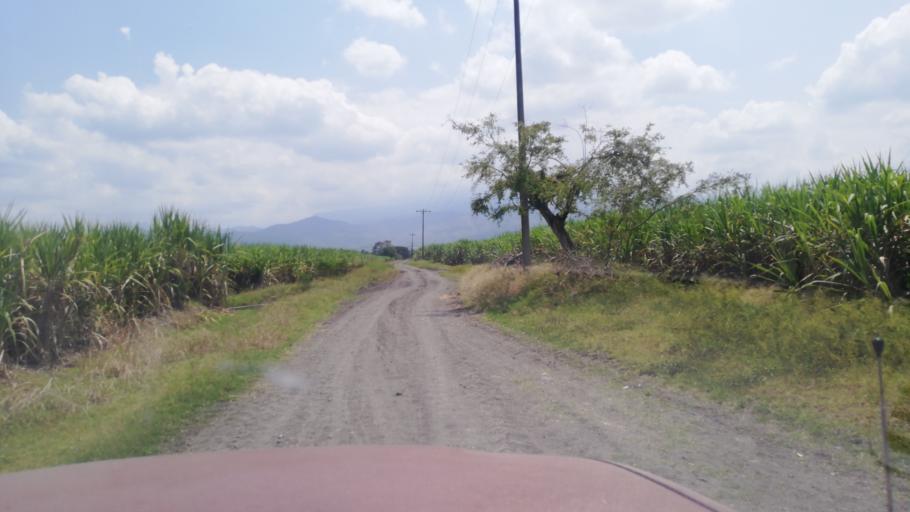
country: CO
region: Valle del Cauca
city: San Pedro
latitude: 3.9953
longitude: -76.2712
